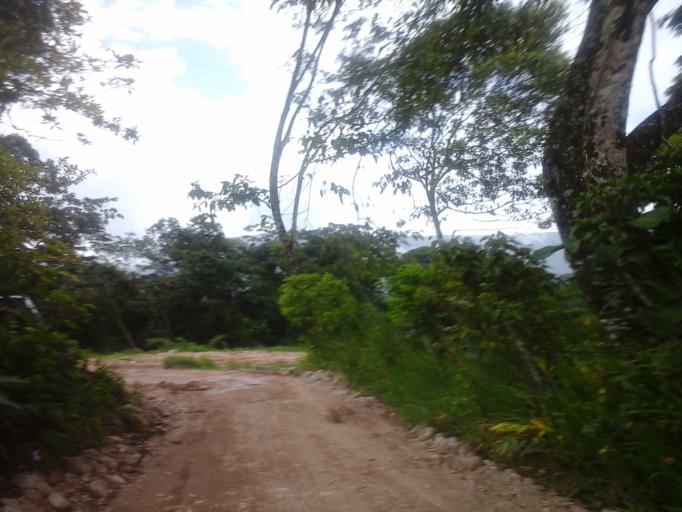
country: CO
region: Putumayo
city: Mocoa
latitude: 1.1729
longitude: -76.6619
